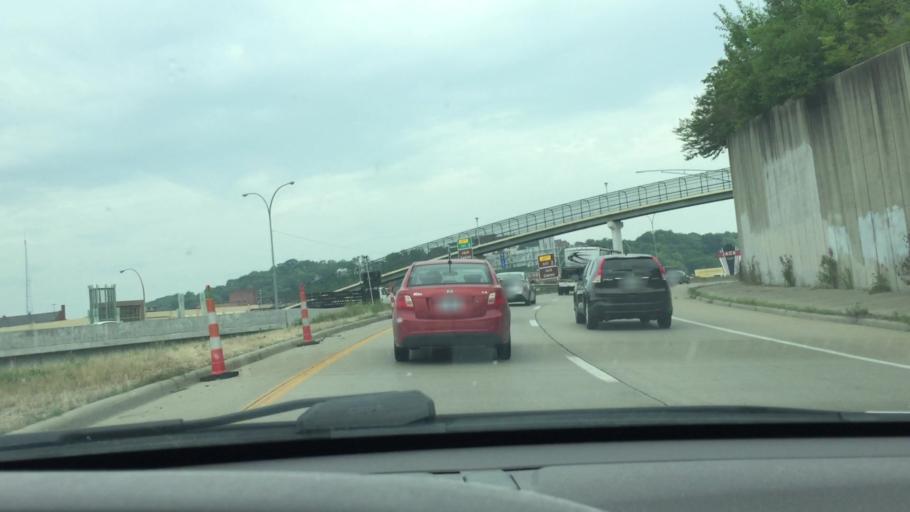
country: US
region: Kentucky
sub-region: Campbell County
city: Newport
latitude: 39.1060
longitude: -84.5033
